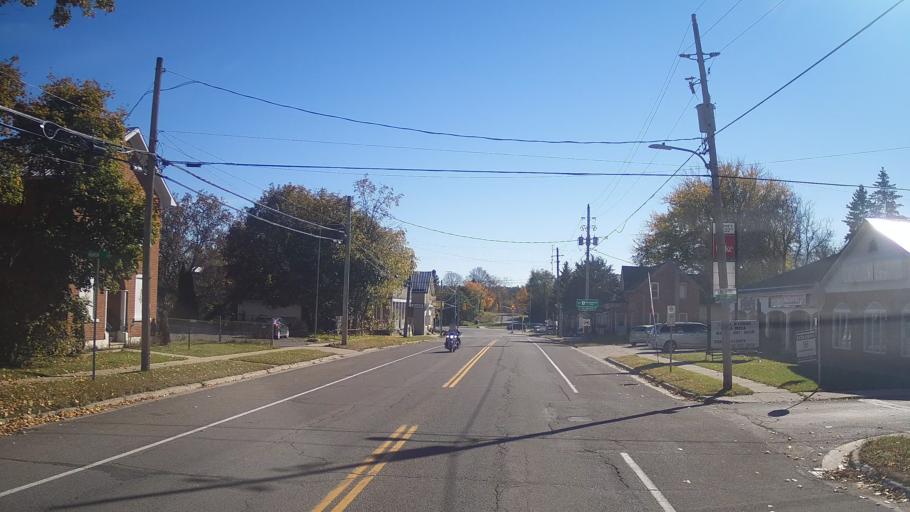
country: CA
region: Ontario
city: Kingston
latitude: 44.4056
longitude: -76.6656
